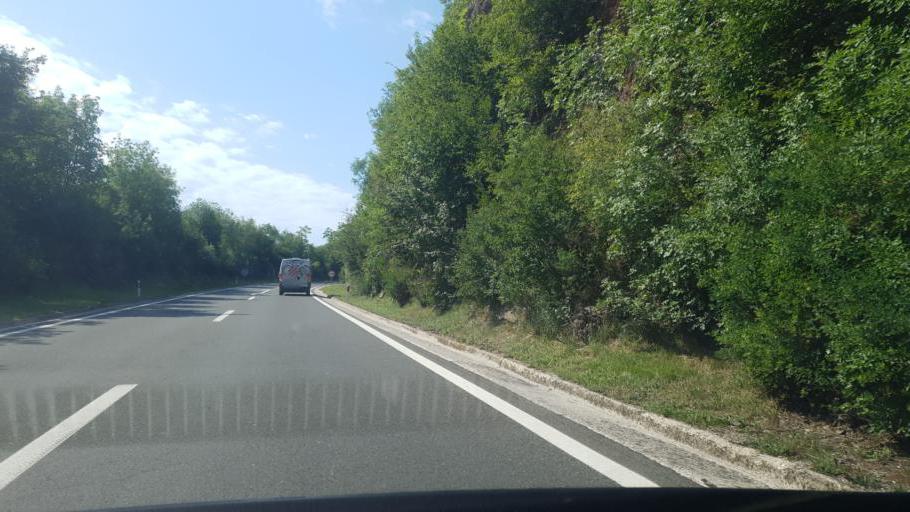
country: HR
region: Primorsko-Goranska
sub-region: Grad Opatija
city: Opatija
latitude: 45.3509
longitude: 14.3065
